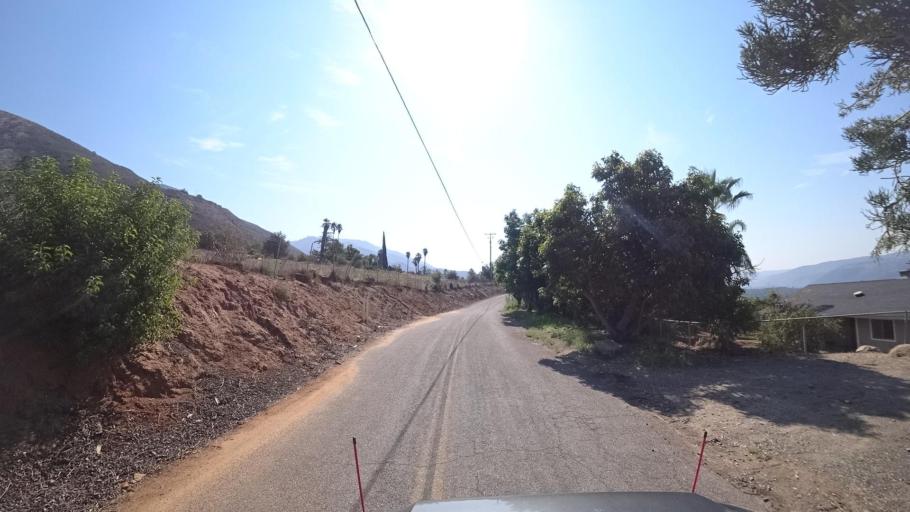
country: US
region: California
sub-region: San Diego County
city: Valley Center
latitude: 33.3412
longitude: -116.9929
